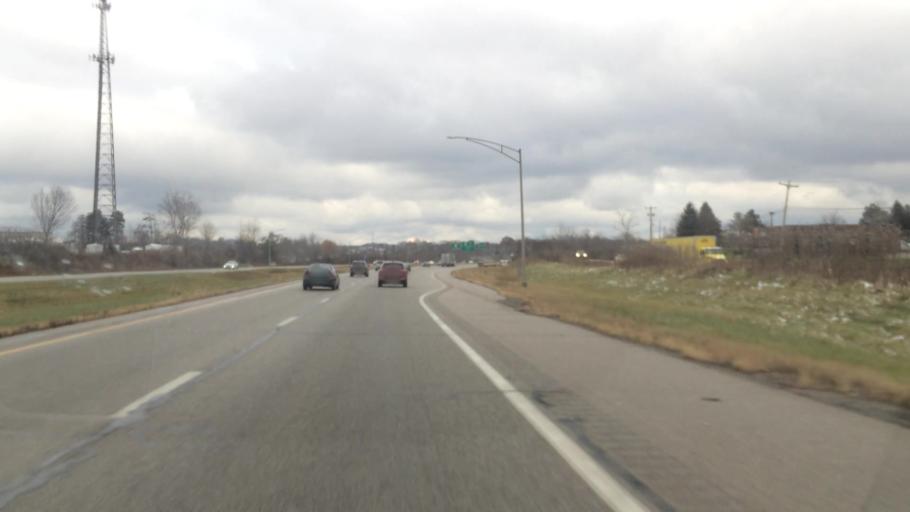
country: US
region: Ohio
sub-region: Portage County
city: Streetsboro
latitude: 41.2642
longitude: -81.3853
